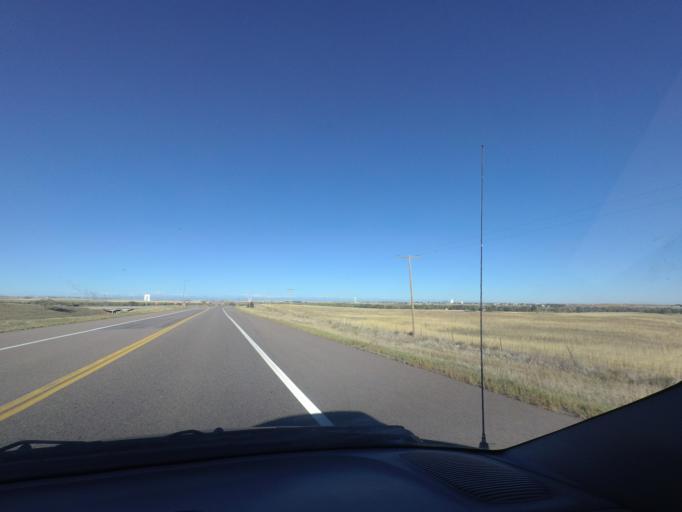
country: US
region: Colorado
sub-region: Adams County
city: Bennett
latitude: 39.7382
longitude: -104.4026
